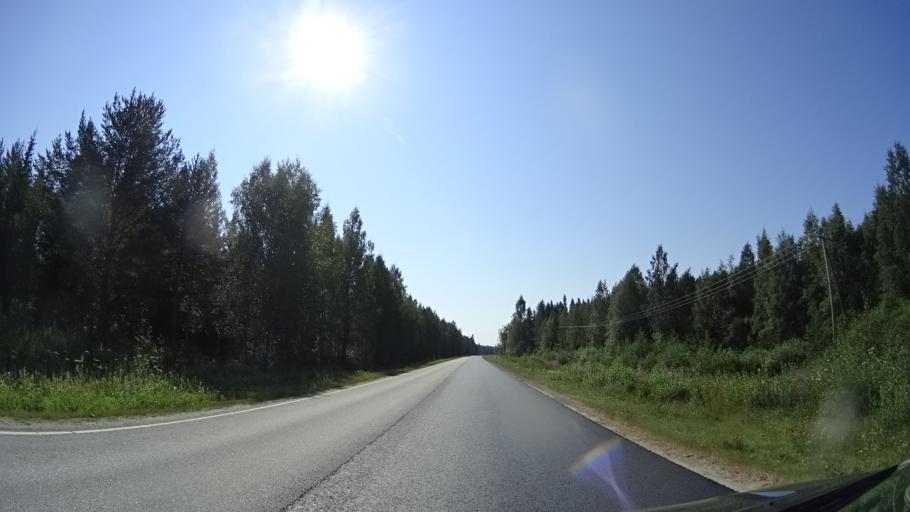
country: FI
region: North Karelia
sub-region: Joensuu
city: Juuka
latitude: 63.2226
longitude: 29.2956
